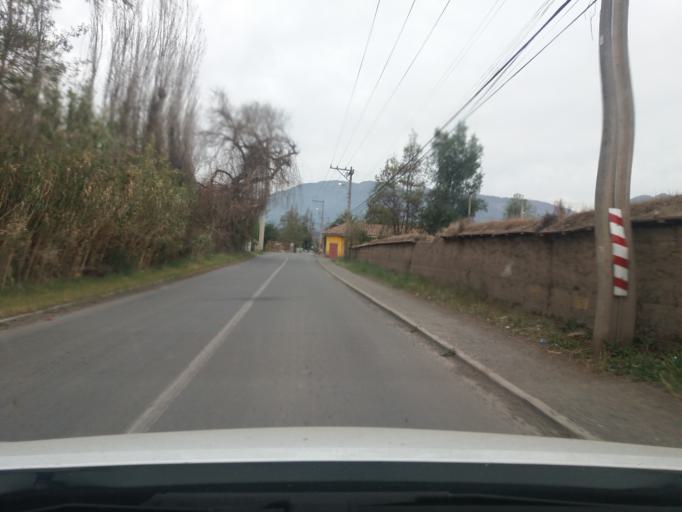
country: CL
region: Valparaiso
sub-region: Provincia de Los Andes
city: Los Andes
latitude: -32.8480
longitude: -70.6280
